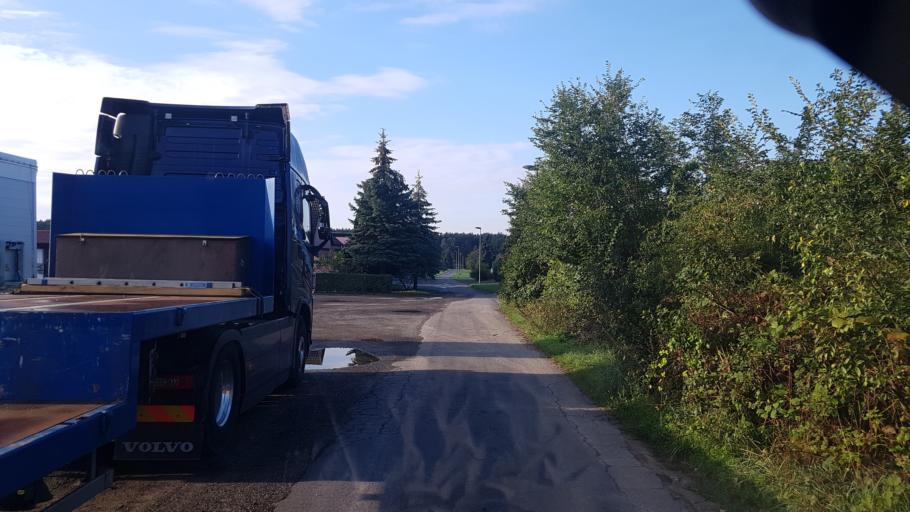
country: DE
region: Brandenburg
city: Bronkow
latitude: 51.6760
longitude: 13.8921
